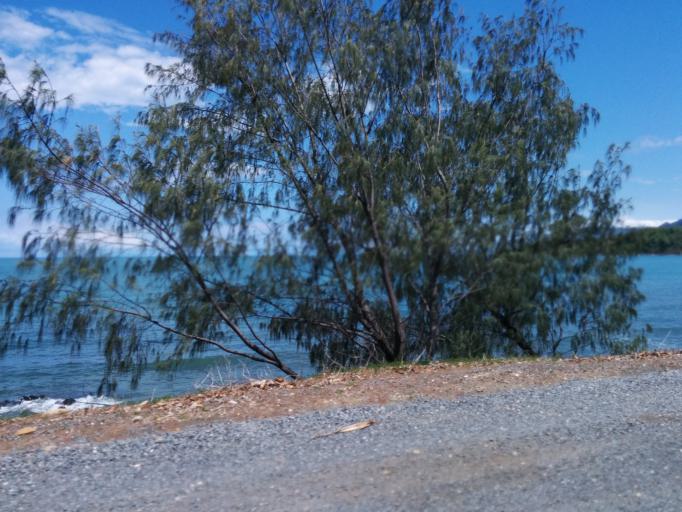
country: AU
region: Queensland
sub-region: Cairns
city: Port Douglas
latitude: -16.5763
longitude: 145.5123
